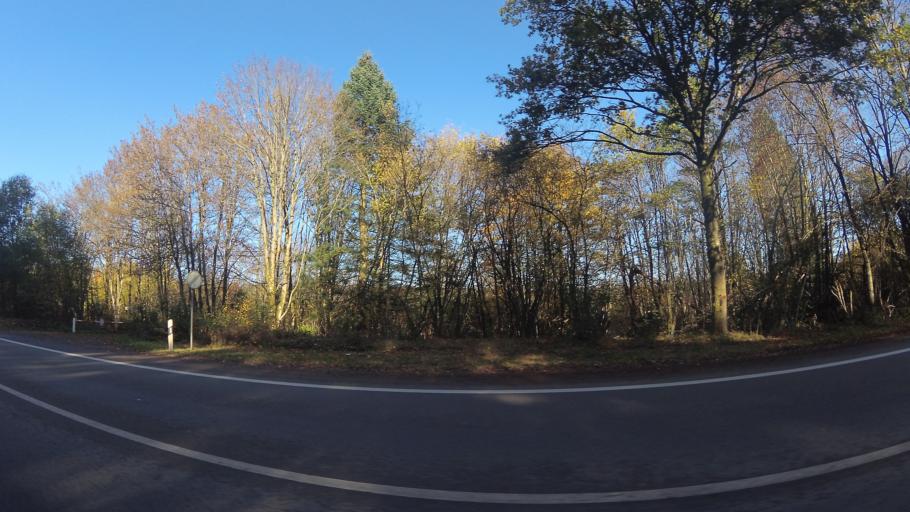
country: DE
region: Saarland
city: Losheim
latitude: 49.5197
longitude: 6.7232
